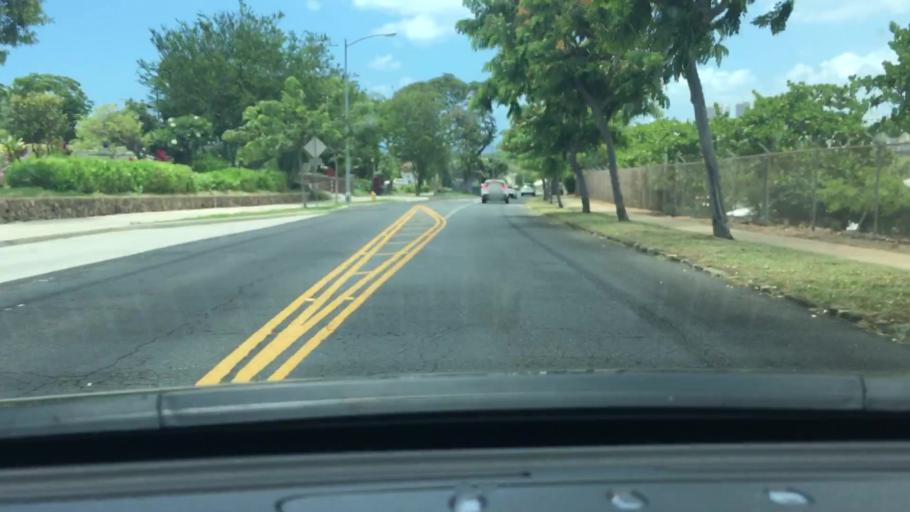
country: US
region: Hawaii
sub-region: Honolulu County
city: Honolulu
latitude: 21.2696
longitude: -157.8061
